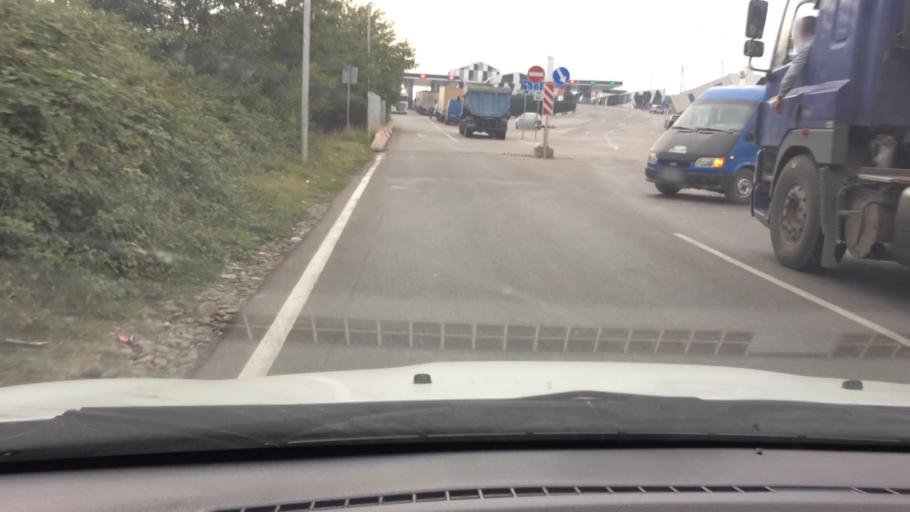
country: AM
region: Tavush
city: Bagratashen
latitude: 41.2284
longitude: 44.8278
